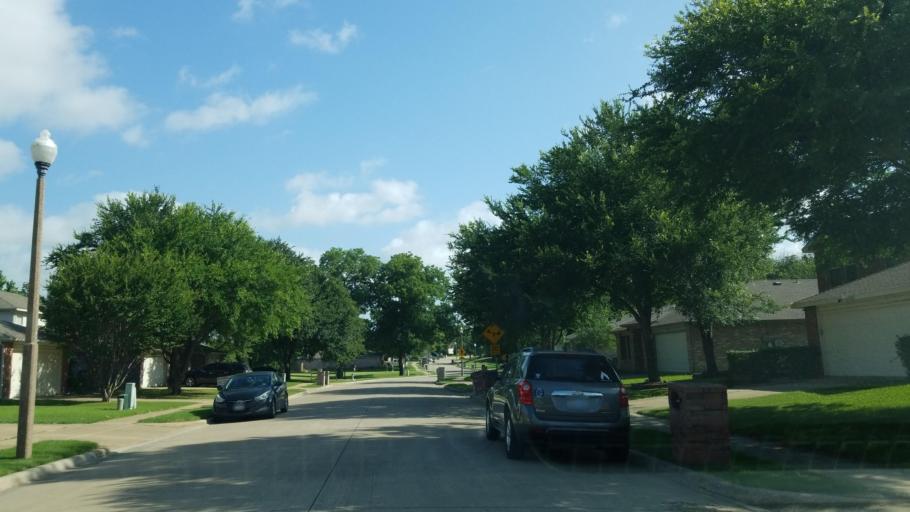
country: US
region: Texas
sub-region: Denton County
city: Copper Canyon
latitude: 33.1408
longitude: -97.1203
